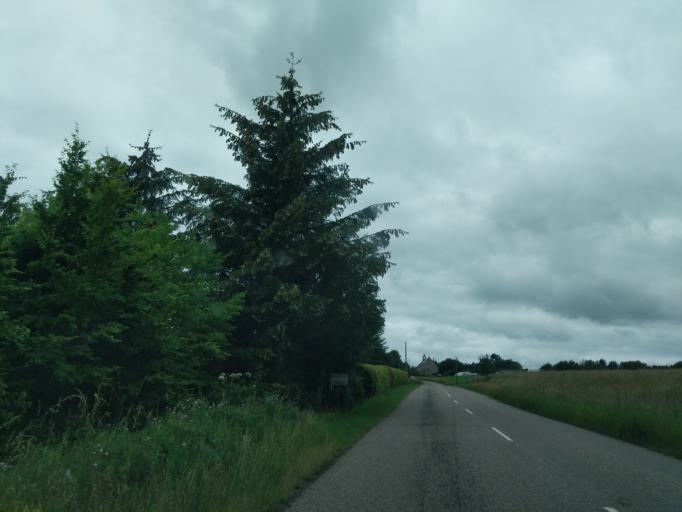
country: GB
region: Scotland
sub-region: Moray
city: Rothes
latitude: 57.4842
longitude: -3.2556
